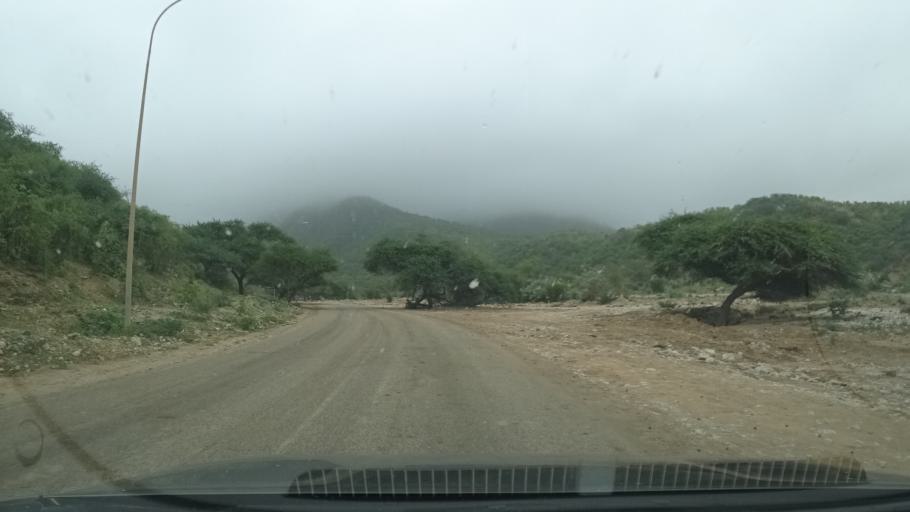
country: OM
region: Zufar
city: Salalah
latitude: 17.0988
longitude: 54.0770
